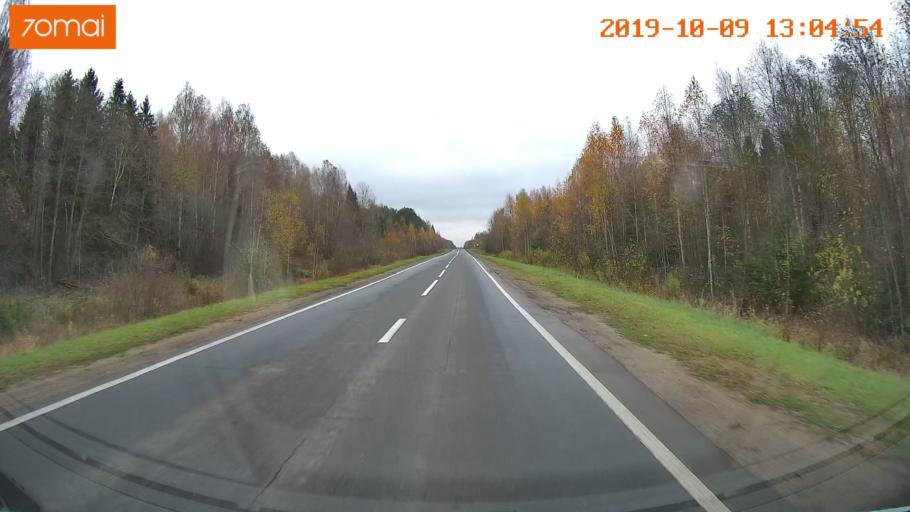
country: RU
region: Jaroslavl
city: Lyubim
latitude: 58.3580
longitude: 40.5662
